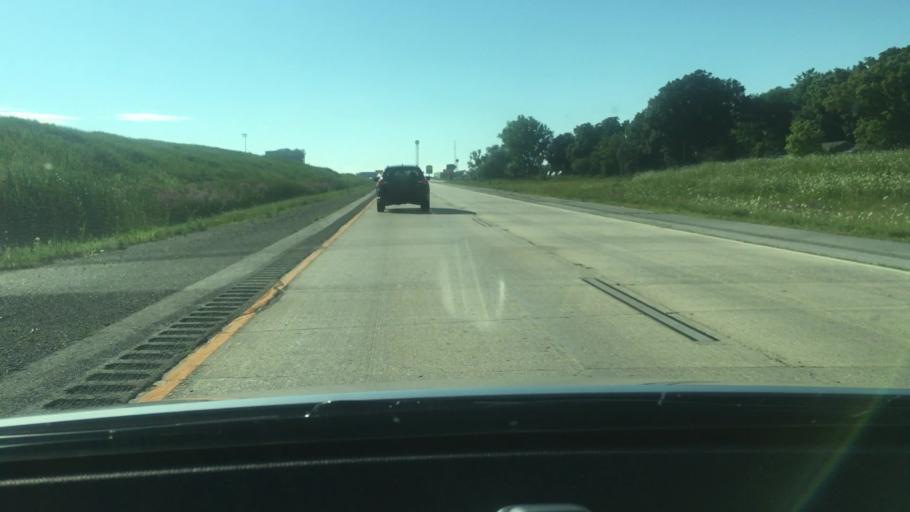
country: US
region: Wisconsin
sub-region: Brown County
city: Ashwaubenon
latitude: 44.4873
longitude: -88.0853
